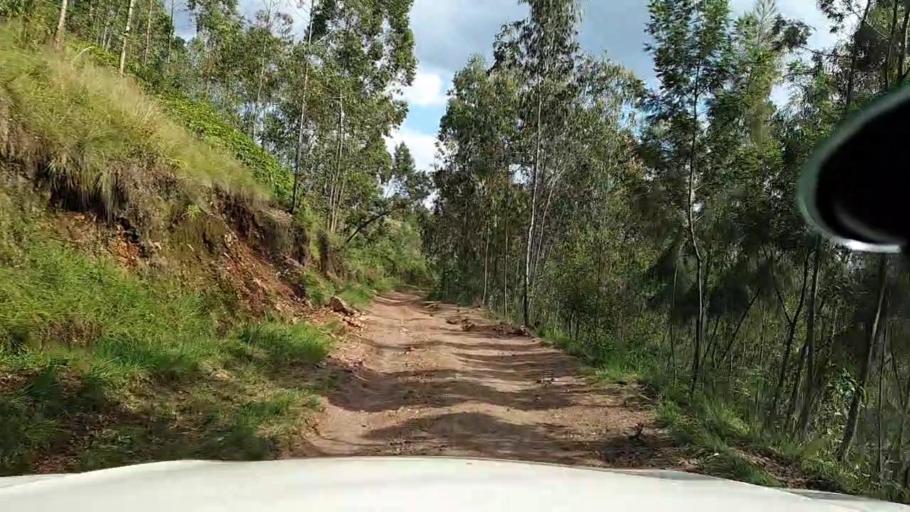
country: RW
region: Kigali
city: Kigali
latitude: -1.7871
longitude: 29.8393
